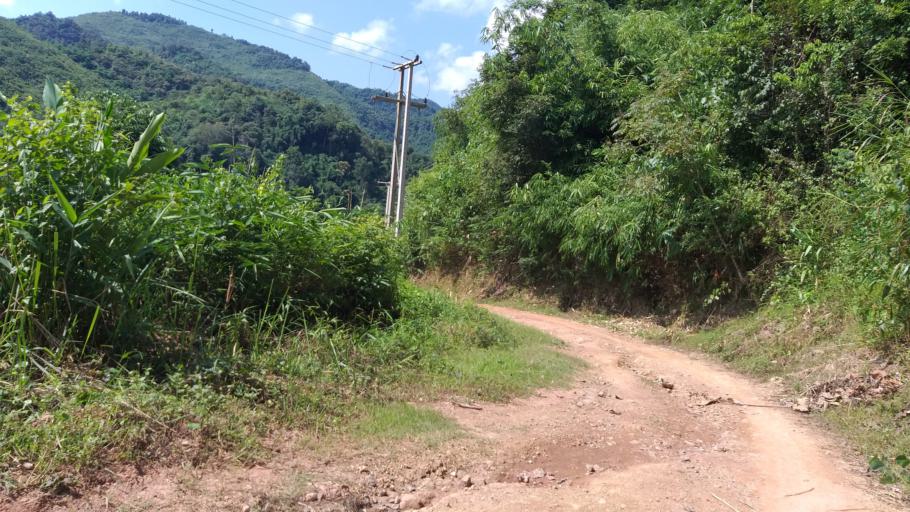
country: LA
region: Phongsali
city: Khoa
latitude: 21.3355
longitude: 102.5632
